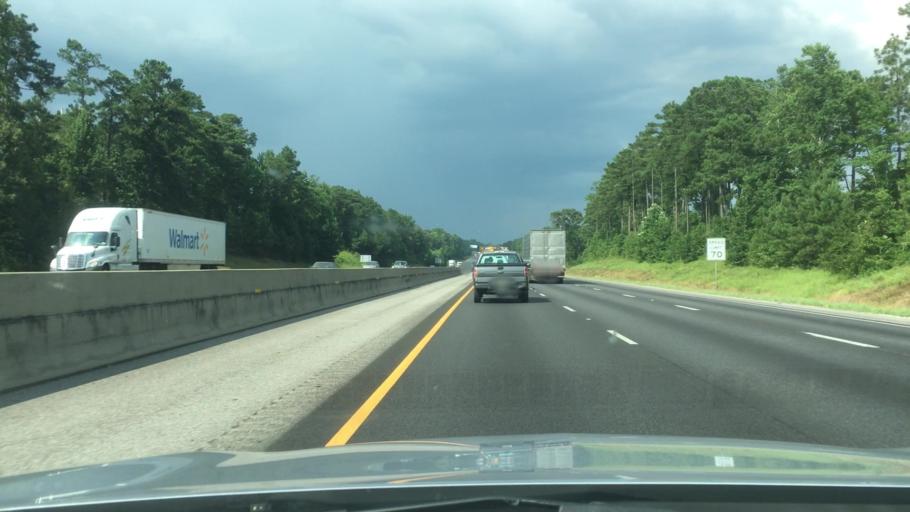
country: US
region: Alabama
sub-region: Tuscaloosa County
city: Vance
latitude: 33.1992
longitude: -87.2350
